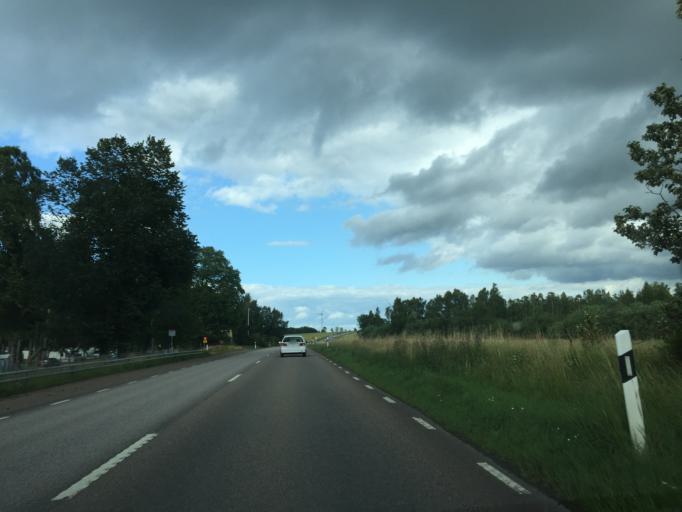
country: SE
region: OEstergoetland
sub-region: Vadstena Kommun
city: Vadstena
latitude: 58.4681
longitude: 14.9400
